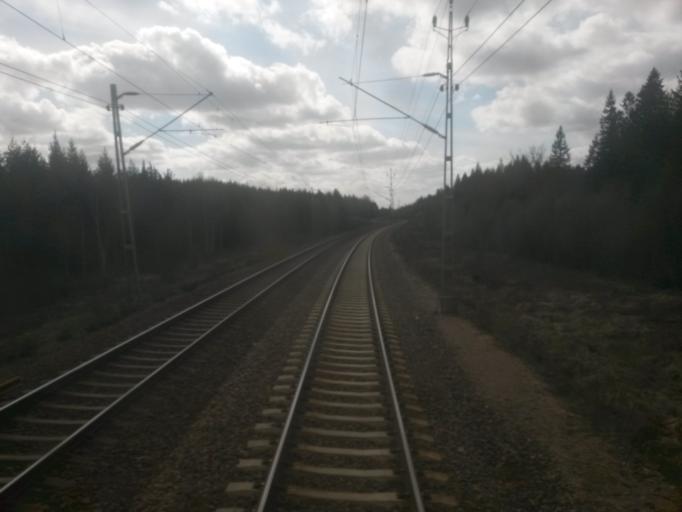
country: SE
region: Vaestra Goetaland
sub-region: Herrljunga Kommun
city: Herrljunga
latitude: 58.0976
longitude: 13.0795
